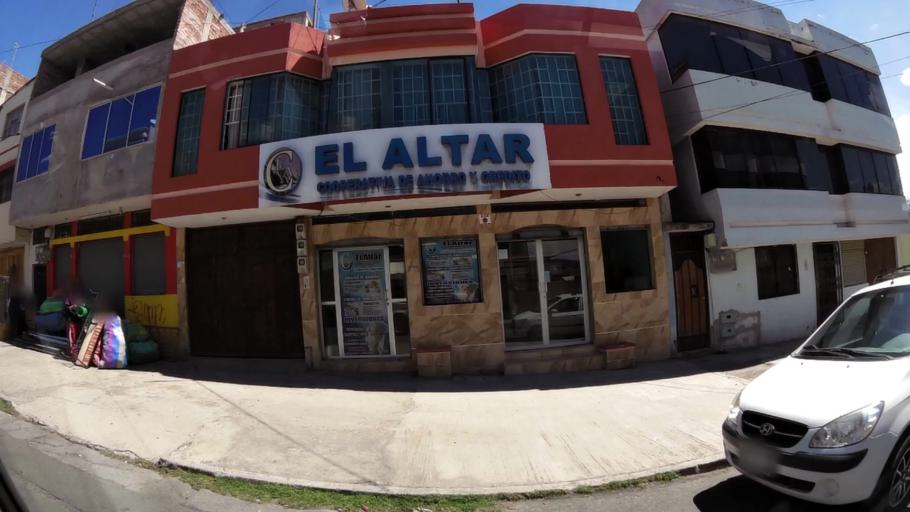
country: EC
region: Chimborazo
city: Riobamba
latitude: -1.6626
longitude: -78.6477
